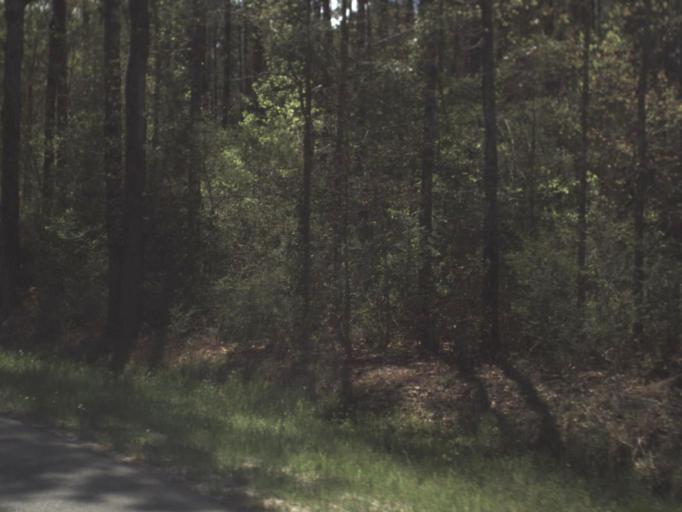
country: US
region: Alabama
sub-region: Geneva County
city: Geneva
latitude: 30.8932
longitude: -85.9531
